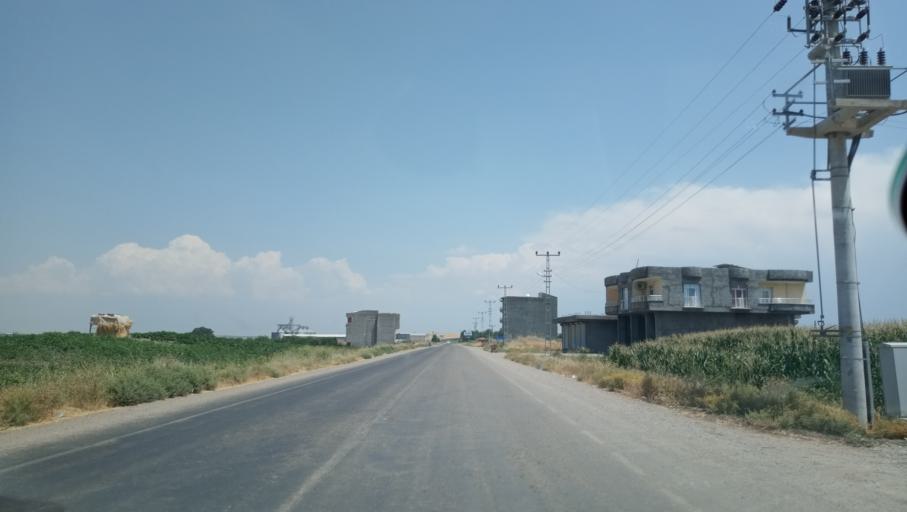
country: TR
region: Diyarbakir
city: Aralik
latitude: 37.8277
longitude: 40.6774
